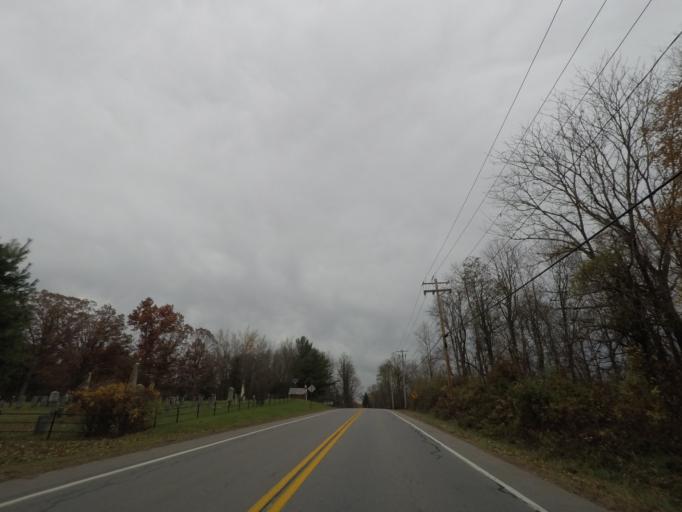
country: US
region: New York
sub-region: Schenectady County
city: Niskayuna
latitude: 42.8273
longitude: -73.8251
